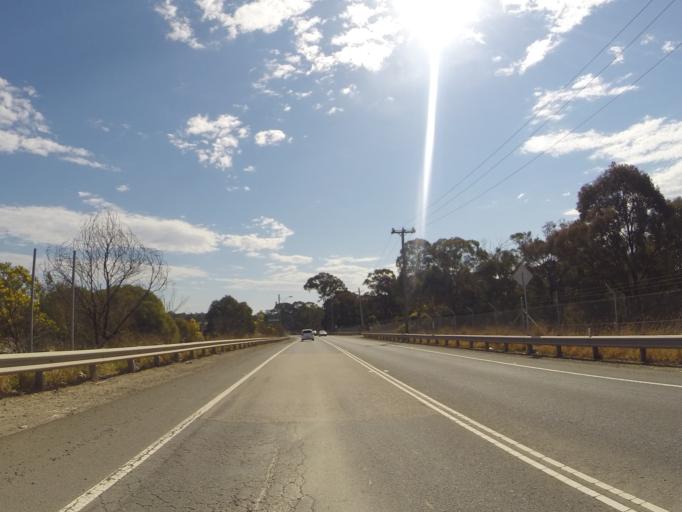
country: AU
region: New South Wales
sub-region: Liverpool
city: Holsworthy
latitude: -33.9629
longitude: 150.9613
